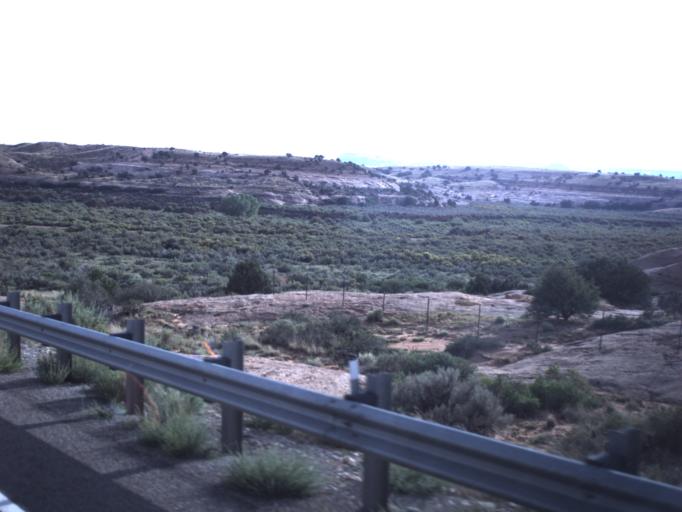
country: US
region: Utah
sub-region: San Juan County
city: Monticello
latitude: 38.2052
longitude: -109.3744
